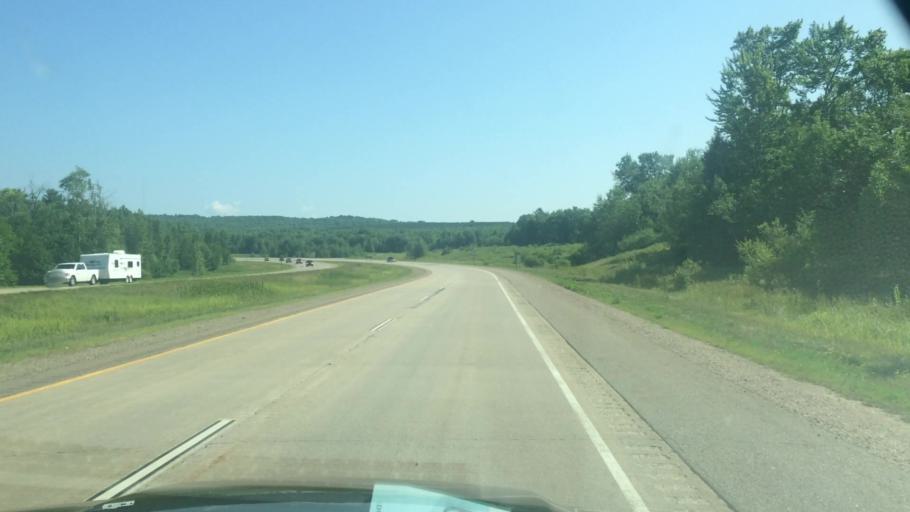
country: US
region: Wisconsin
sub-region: Lincoln County
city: Tomahawk
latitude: 45.3334
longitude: -89.6700
